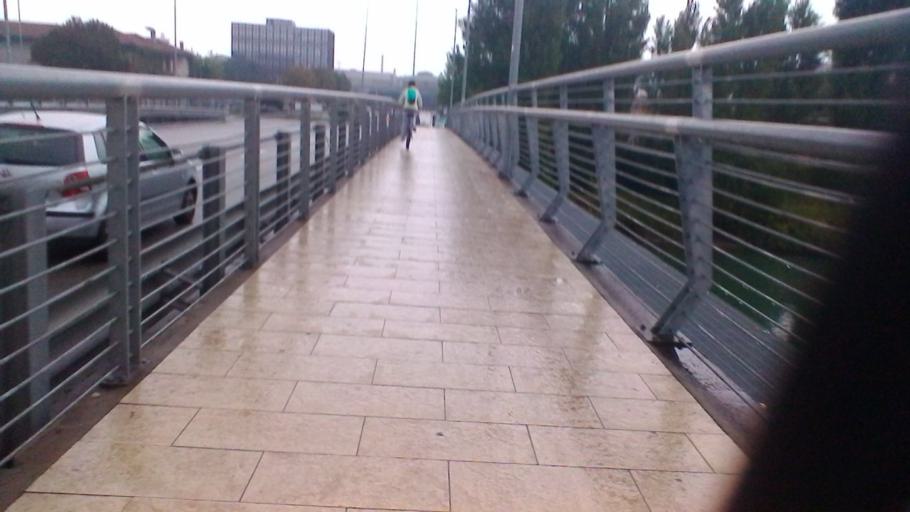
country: IT
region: Veneto
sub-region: Provincia di Verona
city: Verona
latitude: 45.4299
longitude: 10.9971
